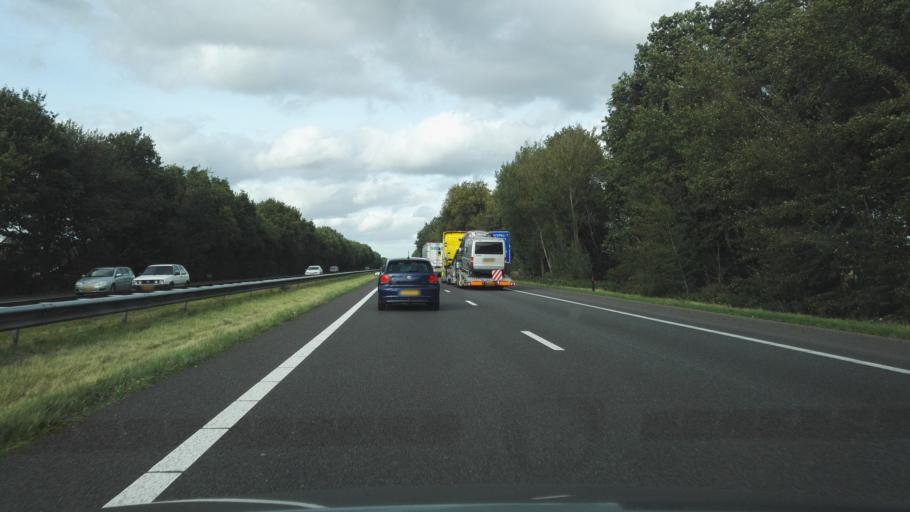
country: NL
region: Gelderland
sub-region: Gemeente Barneveld
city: Barneveld
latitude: 52.1376
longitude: 5.5620
